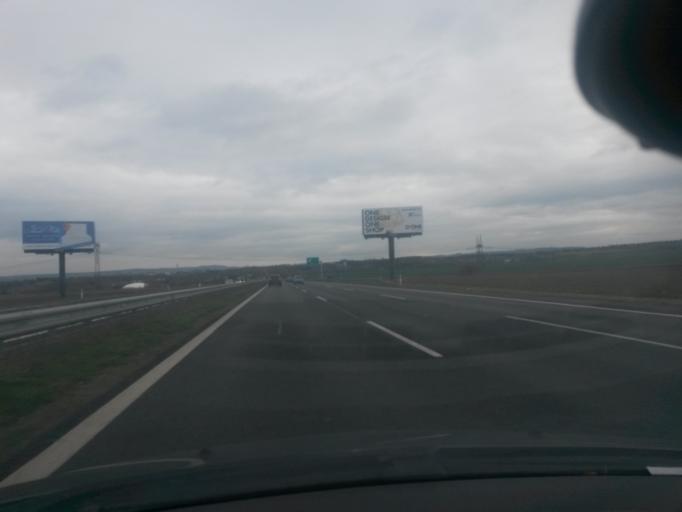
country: CZ
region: Central Bohemia
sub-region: Okres Praha-Zapad
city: Pruhonice
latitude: 50.0138
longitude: 14.5307
